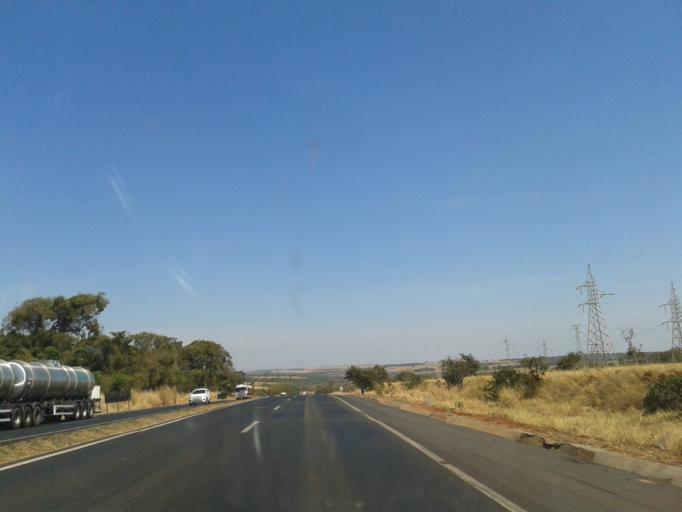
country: BR
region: Minas Gerais
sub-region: Monte Alegre De Minas
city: Monte Alegre de Minas
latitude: -18.7757
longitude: -49.0751
